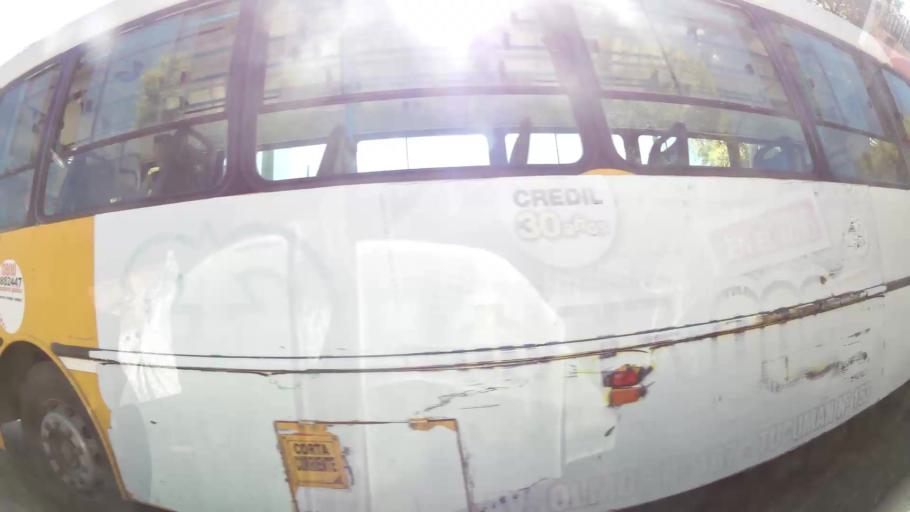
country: AR
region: Cordoba
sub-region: Departamento de Capital
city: Cordoba
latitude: -31.3668
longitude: -64.1382
